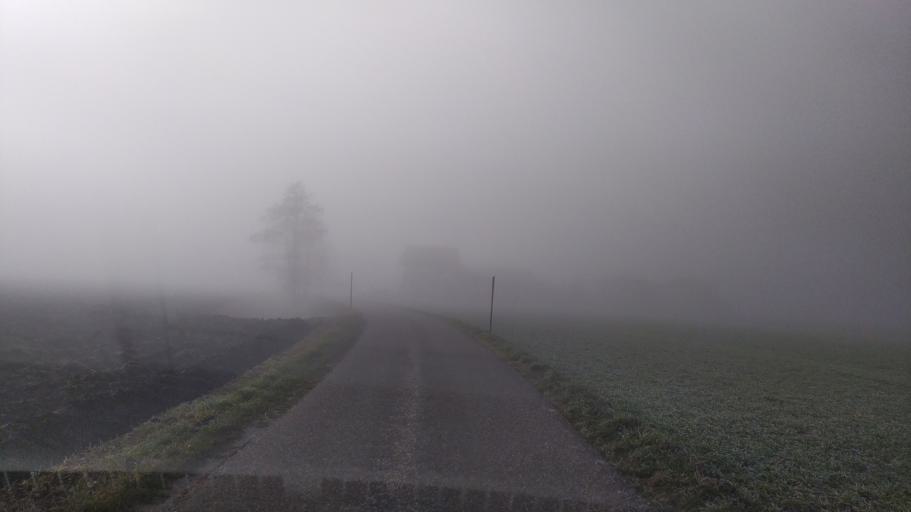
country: AT
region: Upper Austria
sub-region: Politischer Bezirk Urfahr-Umgebung
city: Walding
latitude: 48.3443
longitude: 14.1590
